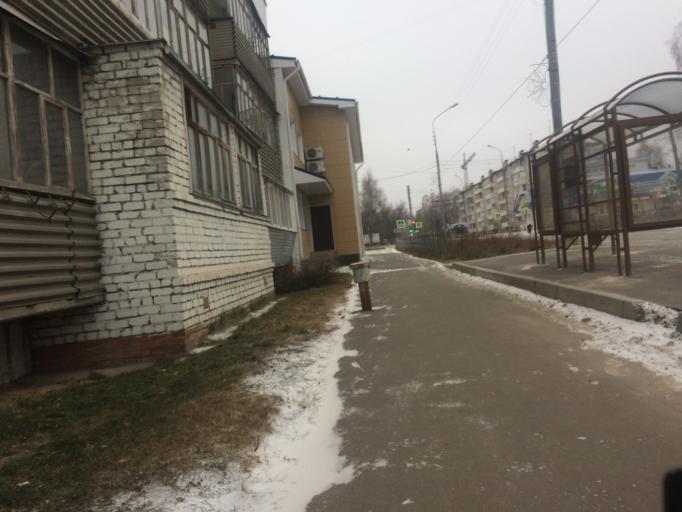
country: RU
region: Mariy-El
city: Yoshkar-Ola
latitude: 56.6505
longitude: 47.8640
